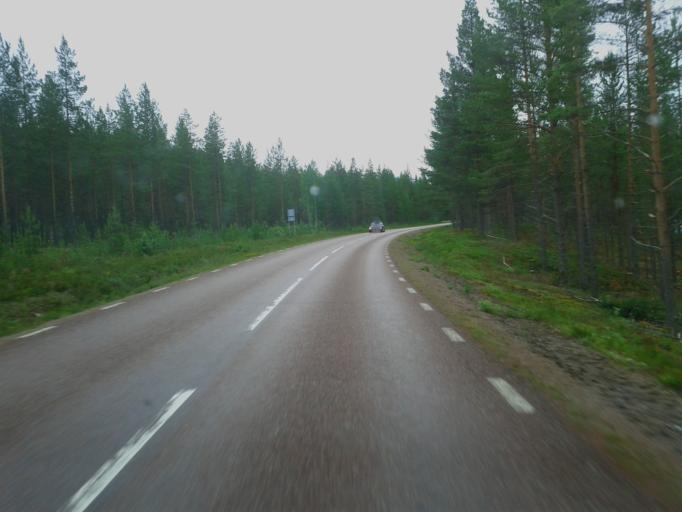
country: NO
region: Hedmark
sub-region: Trysil
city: Innbygda
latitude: 61.7892
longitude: 12.9287
